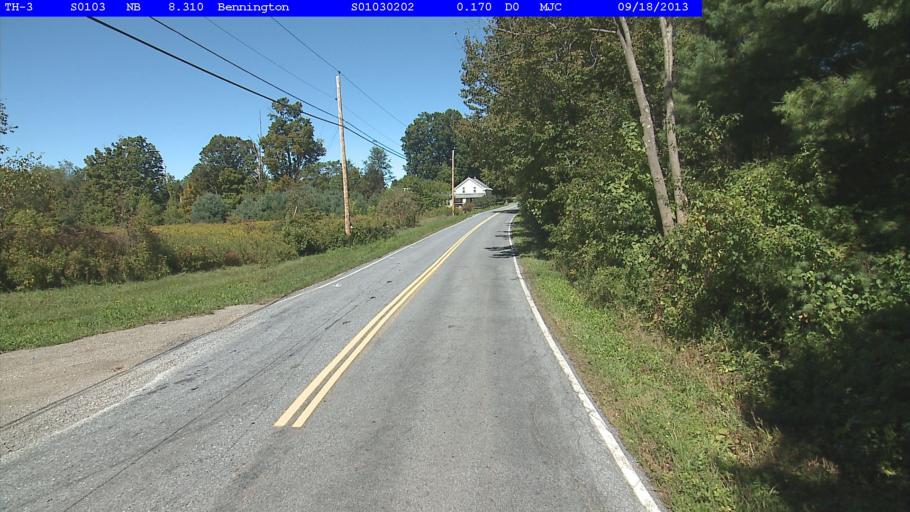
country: US
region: Vermont
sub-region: Bennington County
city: Bennington
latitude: 42.8392
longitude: -73.1716
